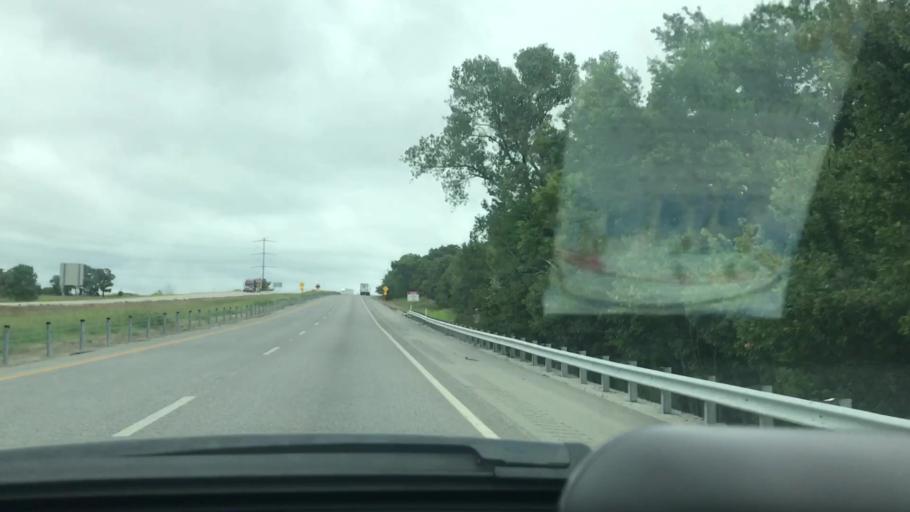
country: US
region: Oklahoma
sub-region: Pittsburg County
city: McAlester
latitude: 34.6731
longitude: -95.9356
